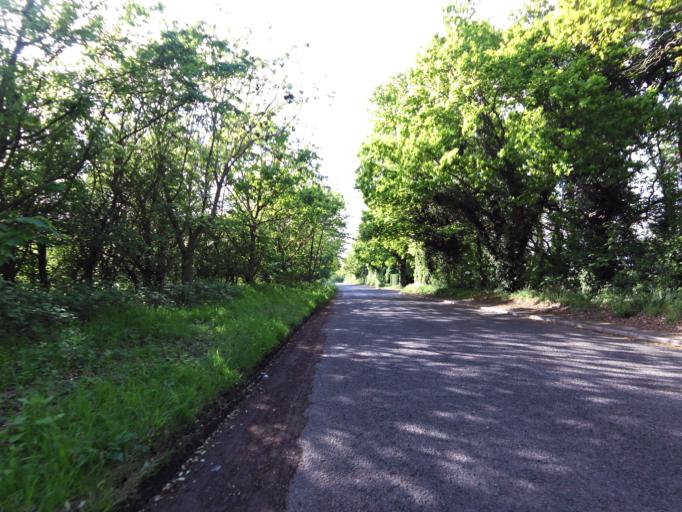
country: GB
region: England
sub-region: Suffolk
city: Beccles
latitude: 52.4508
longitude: 1.6079
